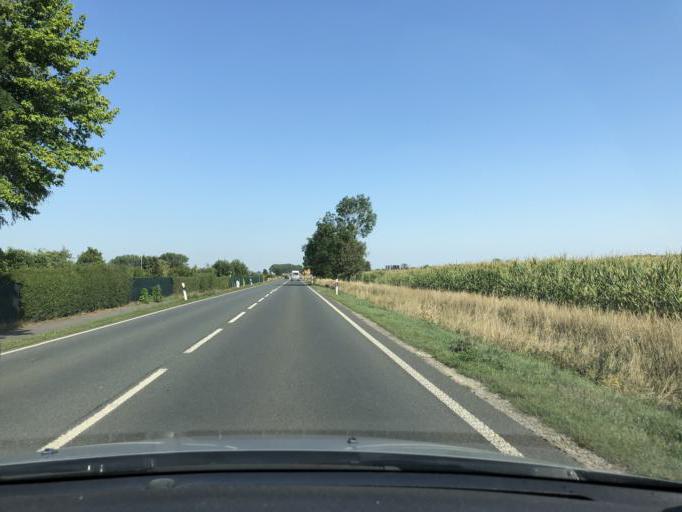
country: DE
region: Thuringia
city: Soemmerda
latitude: 51.1589
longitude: 11.1515
